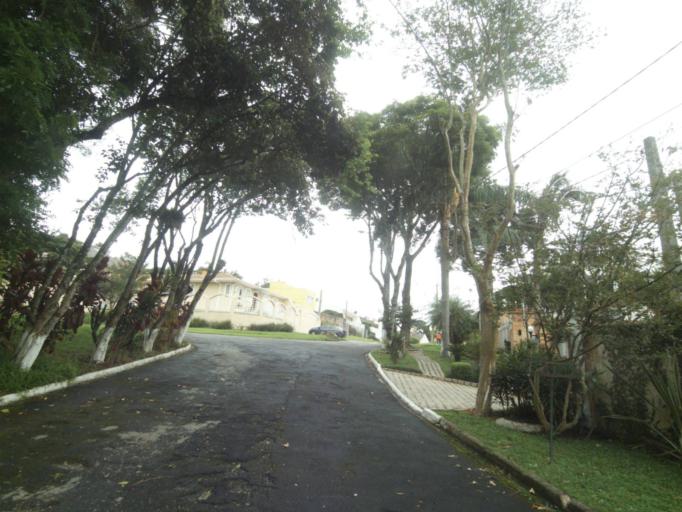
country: BR
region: Parana
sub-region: Curitiba
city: Curitiba
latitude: -25.4080
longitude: -49.2893
